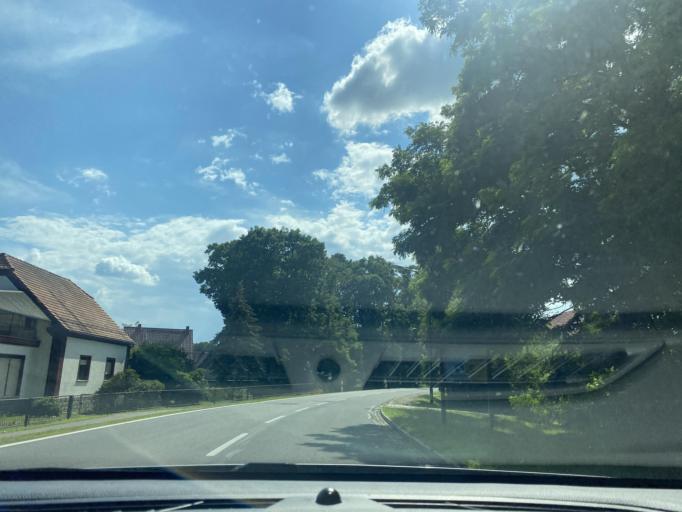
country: DE
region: Saxony
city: Boxberg
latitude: 51.4095
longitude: 14.5798
